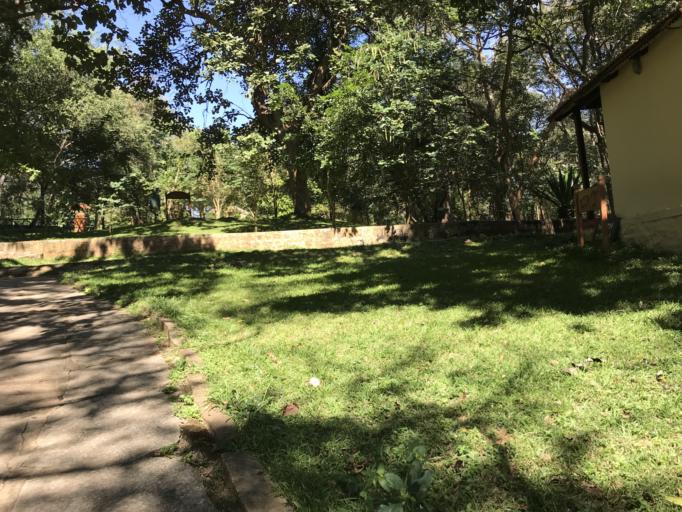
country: IN
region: Karnataka
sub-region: Mysore
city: Sargur
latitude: 11.9371
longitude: 76.2706
